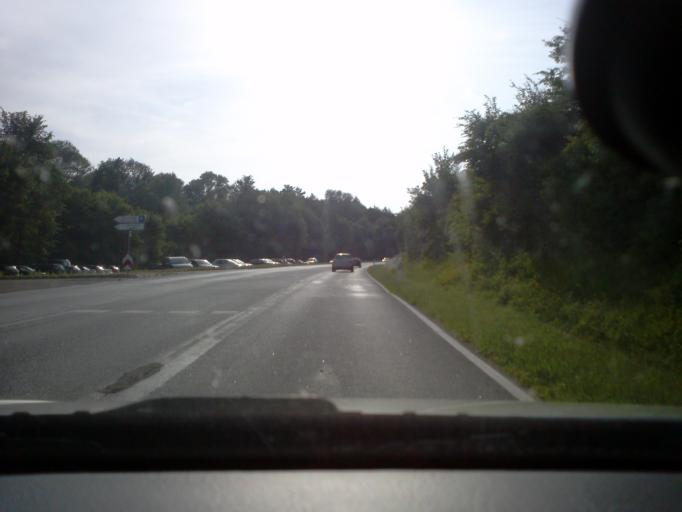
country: DE
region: Baden-Wuerttemberg
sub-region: Regierungsbezirk Stuttgart
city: Zaberfeld
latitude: 49.0603
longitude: 8.9127
